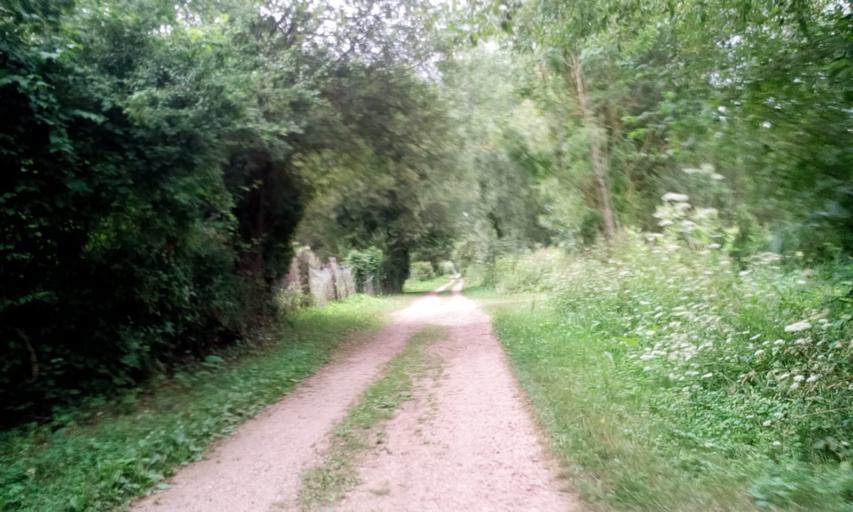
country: FR
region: Lower Normandy
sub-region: Departement du Calvados
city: Bellengreville
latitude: 49.1124
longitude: -0.2124
